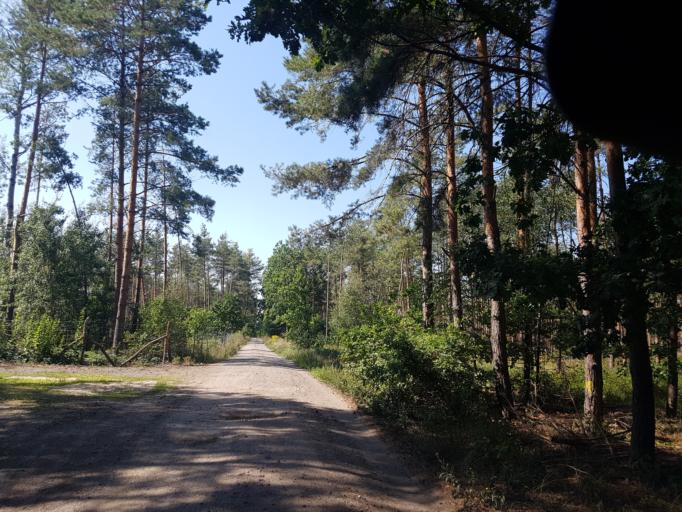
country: DE
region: Brandenburg
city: Elsterwerda
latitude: 51.4874
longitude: 13.4979
